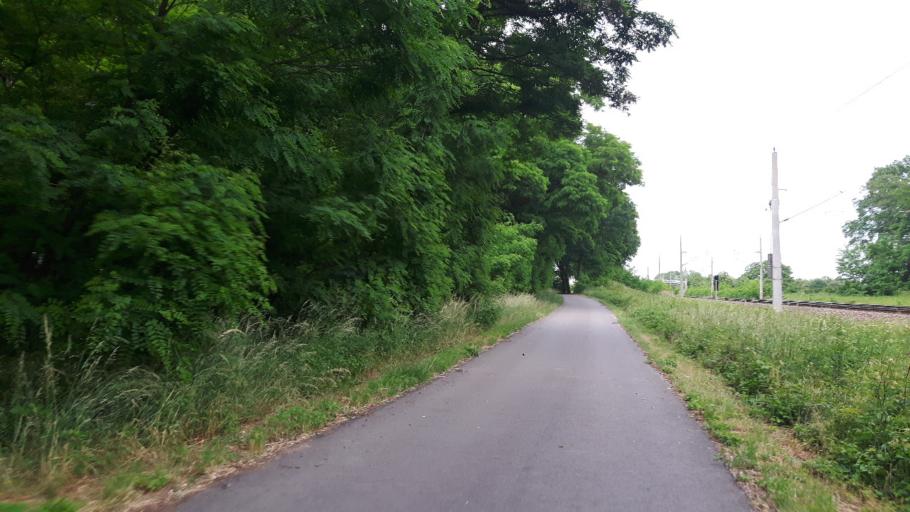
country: DE
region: Saxony-Anhalt
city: Bergwitz
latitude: 51.8249
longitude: 12.6072
